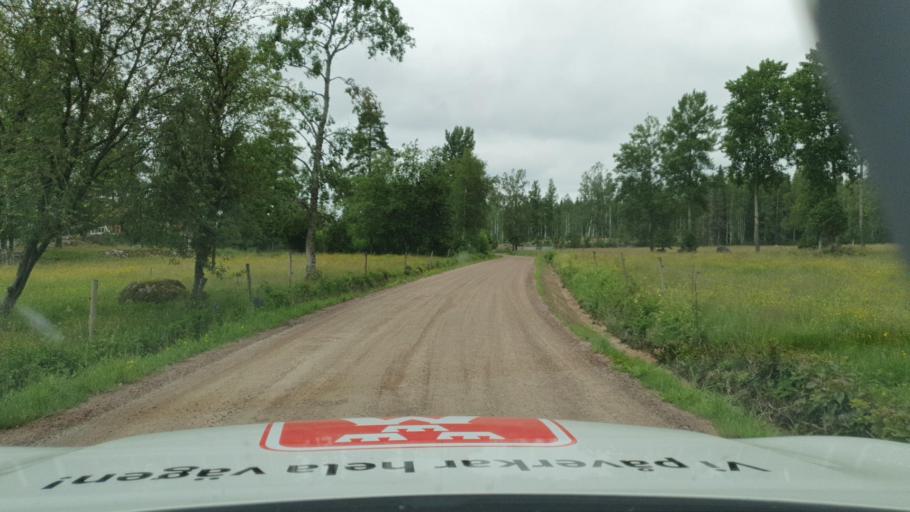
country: SE
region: Vaermland
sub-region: Filipstads Kommun
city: Filipstad
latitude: 59.5667
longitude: 13.9666
